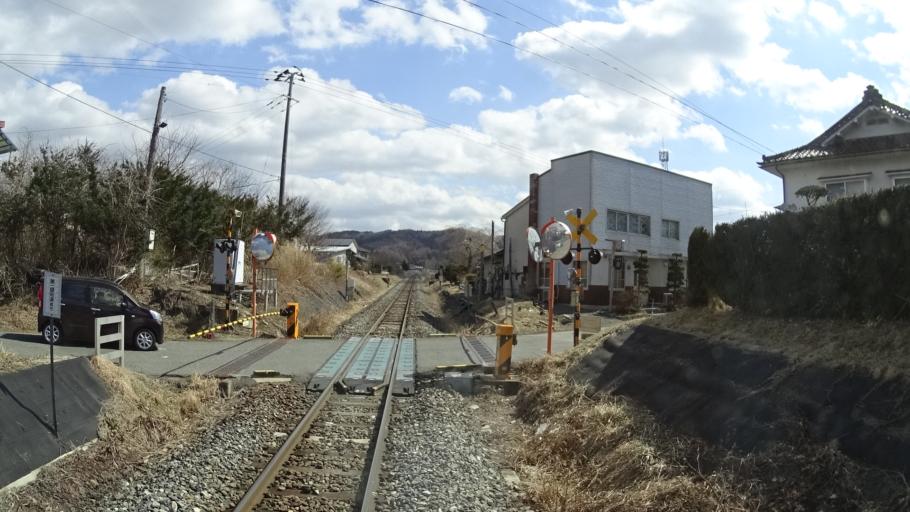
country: JP
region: Iwate
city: Tono
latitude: 39.2824
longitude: 141.5881
